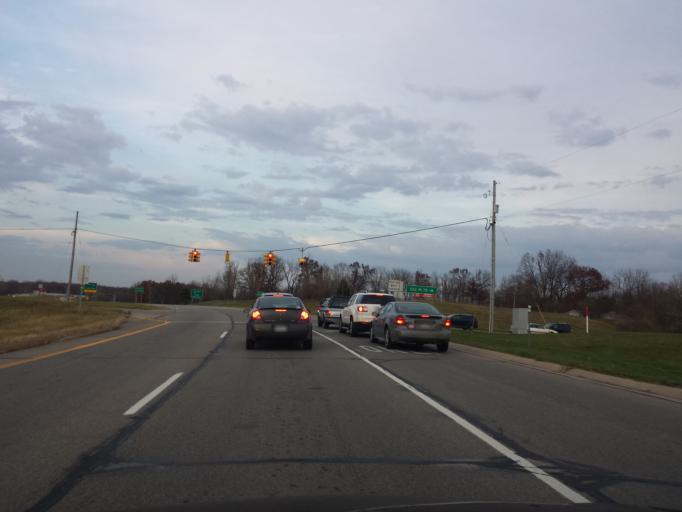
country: US
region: Michigan
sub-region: Ingham County
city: Haslett
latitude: 42.7750
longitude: -84.4105
